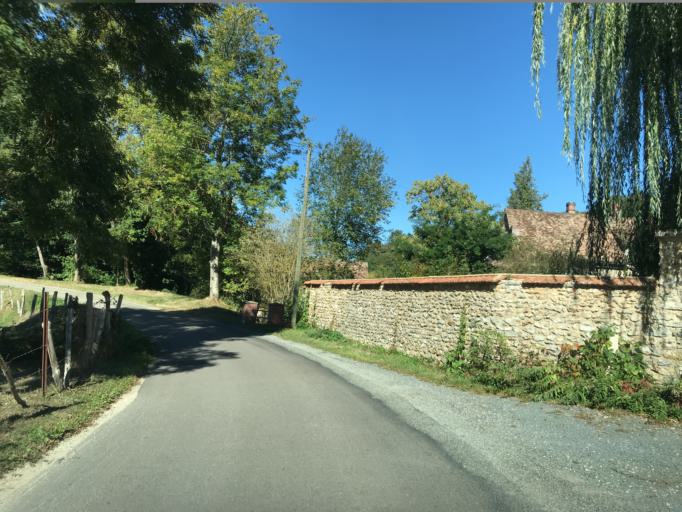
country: FR
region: Haute-Normandie
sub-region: Departement de l'Eure
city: Houlbec-Cocherel
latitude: 49.0996
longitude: 1.3406
